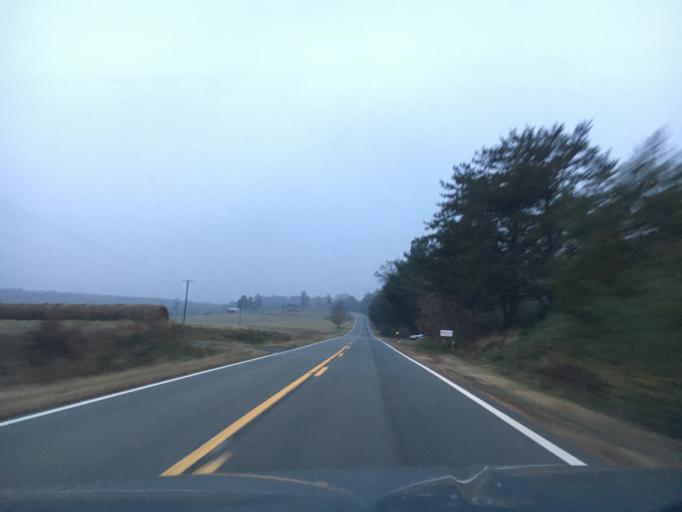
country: US
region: Virginia
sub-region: Halifax County
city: South Boston
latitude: 36.7023
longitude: -78.9557
